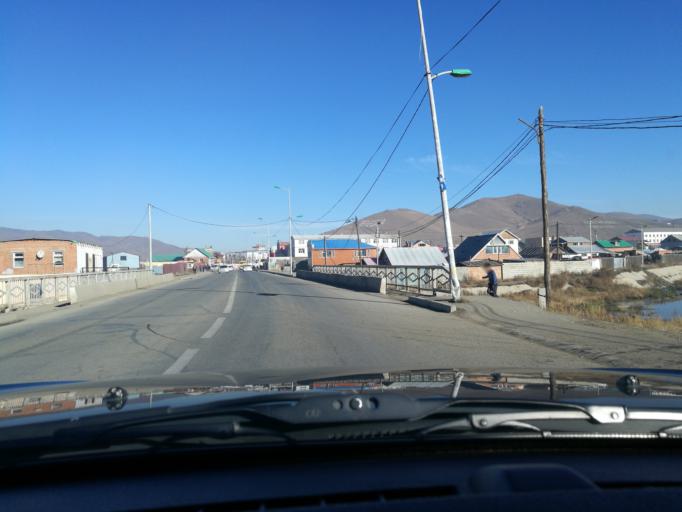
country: MN
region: Ulaanbaatar
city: Ulaanbaatar
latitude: 47.9785
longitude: 106.9390
